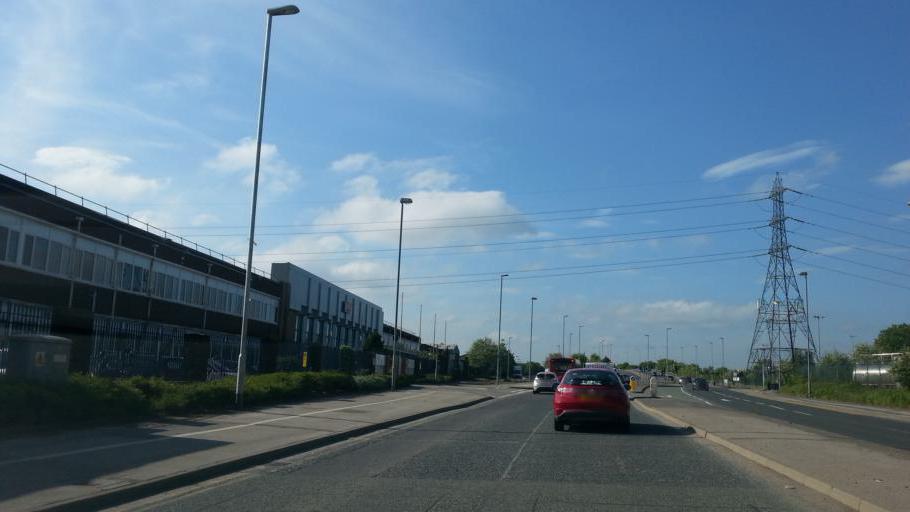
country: GB
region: England
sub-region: Manchester
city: Failsworth
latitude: 53.5311
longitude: -2.1750
